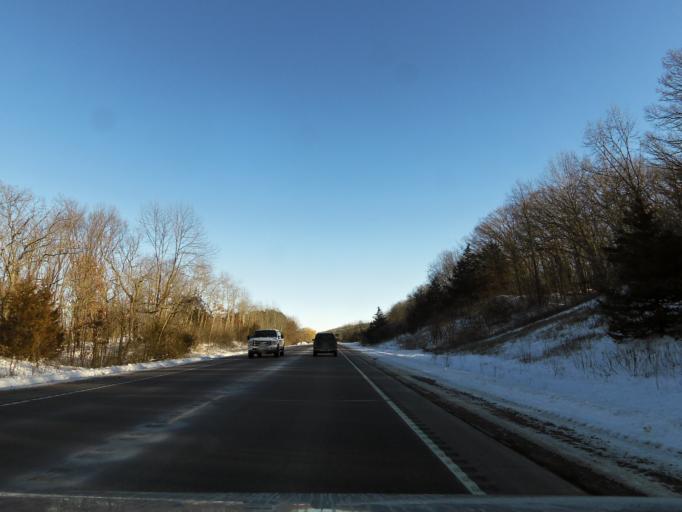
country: US
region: Wisconsin
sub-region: Columbia County
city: Portage
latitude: 43.5082
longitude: -89.5504
